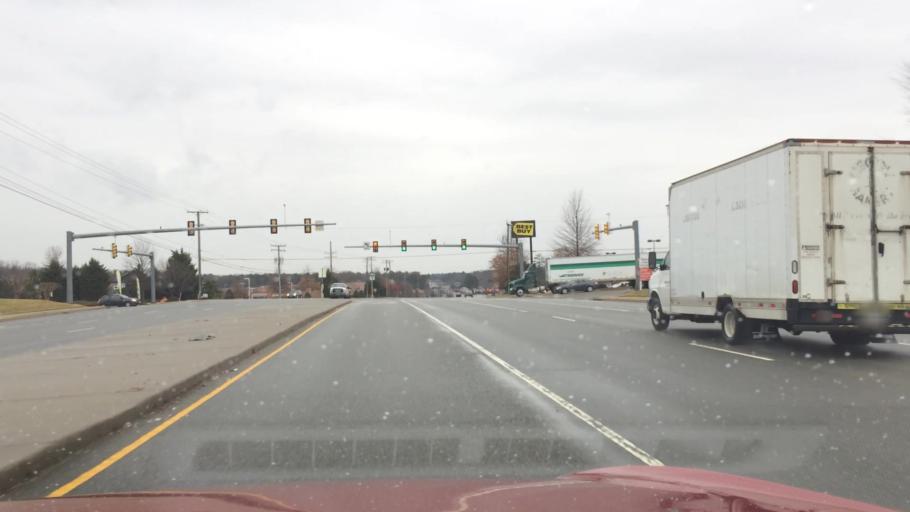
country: US
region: Virginia
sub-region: Henrico County
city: Glen Allen
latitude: 37.6677
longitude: -77.4608
